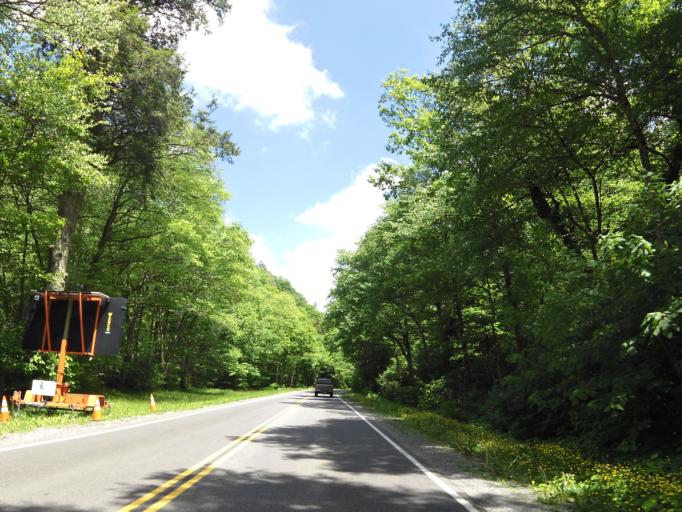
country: US
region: Tennessee
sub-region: Sevier County
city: Gatlinburg
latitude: 35.6246
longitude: -83.4469
